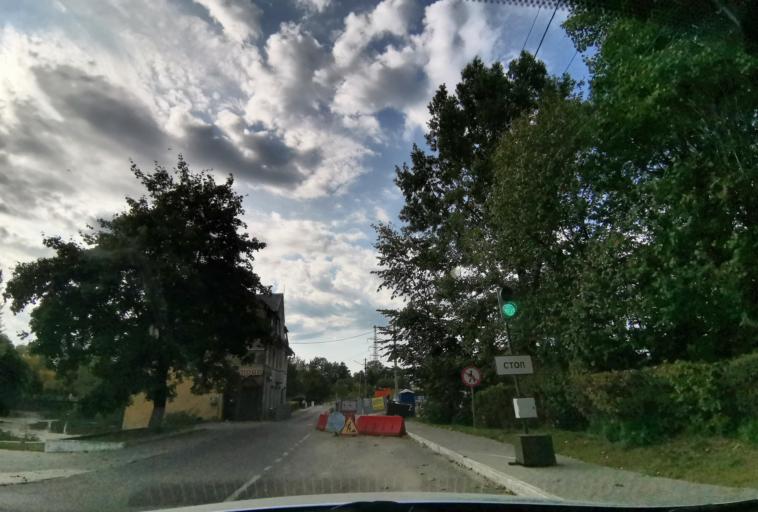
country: RU
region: Kaliningrad
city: Neman
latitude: 55.0397
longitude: 22.0255
